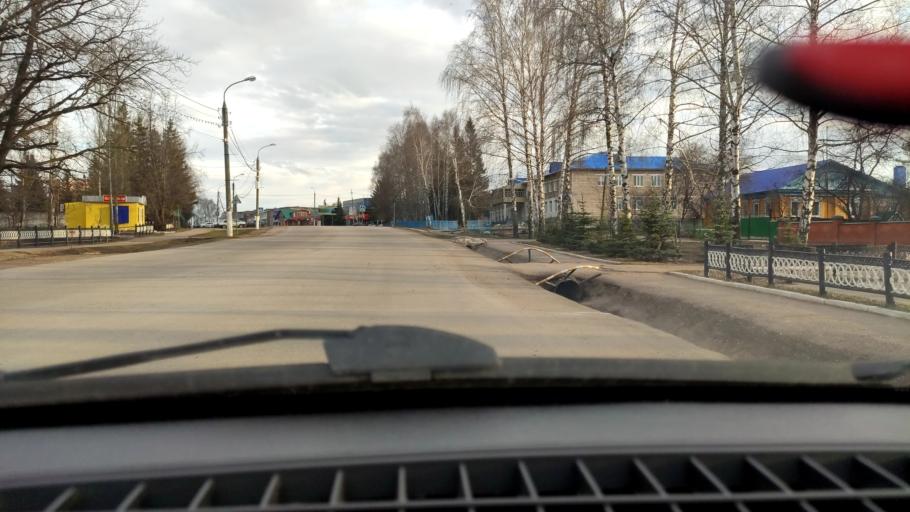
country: RU
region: Bashkortostan
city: Tolbazy
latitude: 54.0127
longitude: 55.8863
